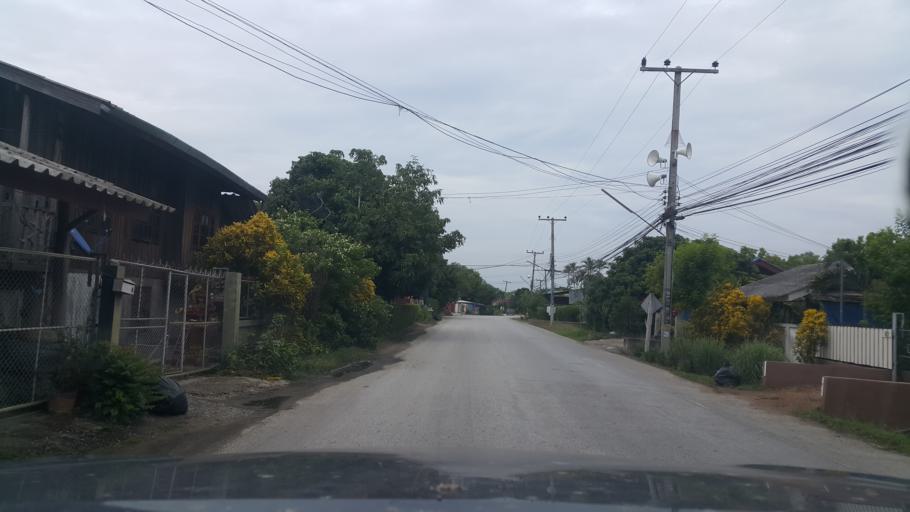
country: TH
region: Chiang Mai
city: San Pa Tong
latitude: 18.6497
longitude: 98.8385
